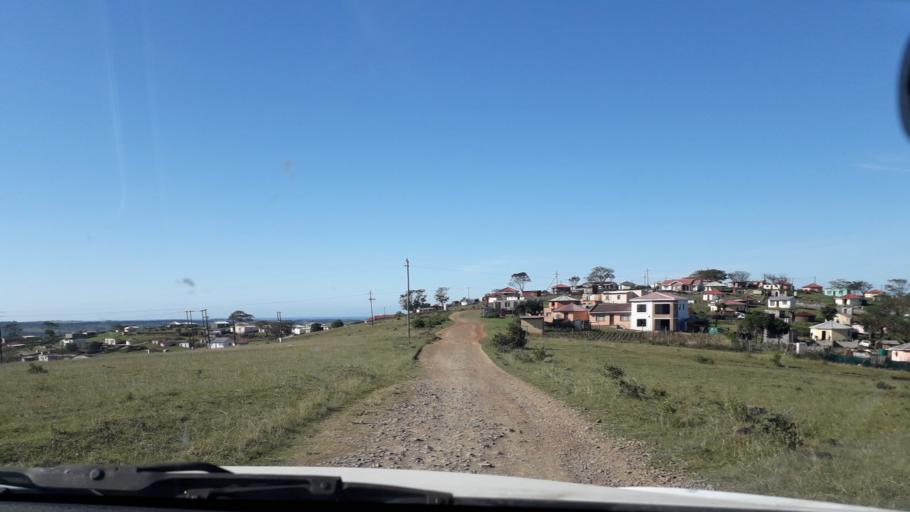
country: ZA
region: Eastern Cape
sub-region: Buffalo City Metropolitan Municipality
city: East London
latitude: -32.8413
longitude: 27.9844
